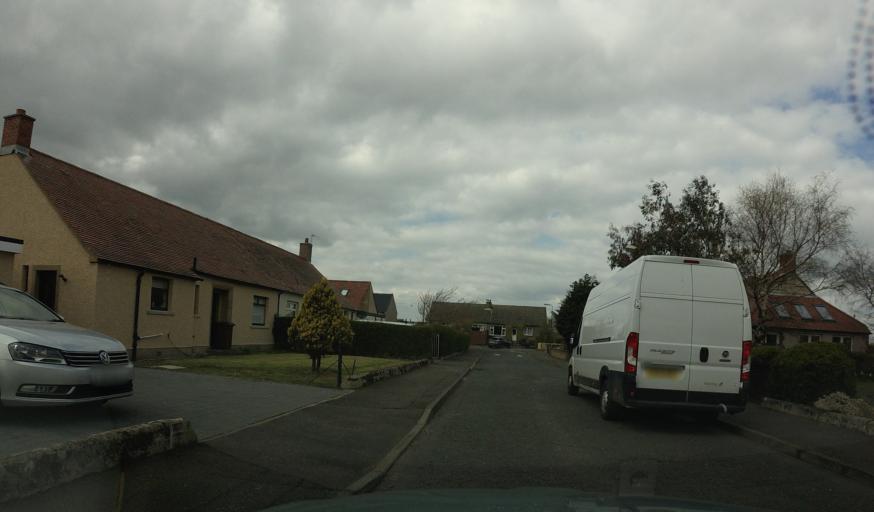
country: GB
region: Scotland
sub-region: Midlothian
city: Gorebridge
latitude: 55.8209
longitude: -3.0234
